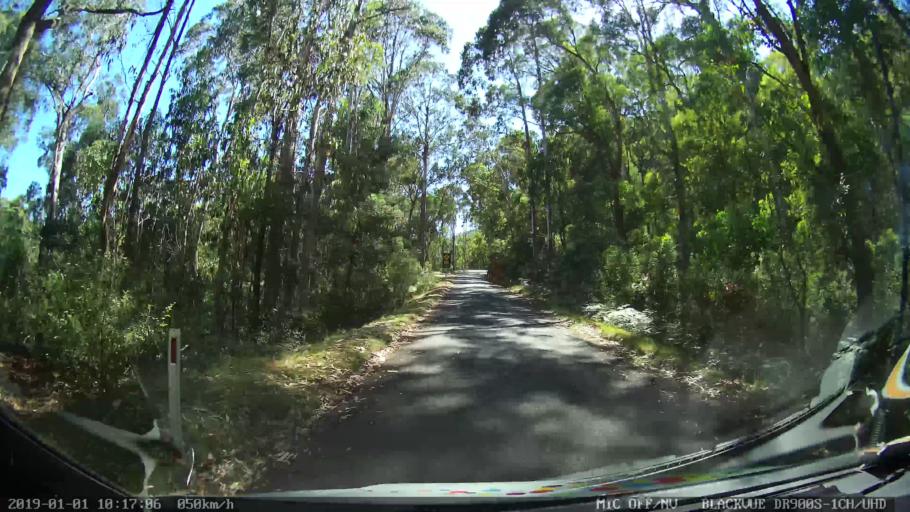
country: AU
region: New South Wales
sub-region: Snowy River
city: Jindabyne
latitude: -36.0917
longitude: 148.1732
